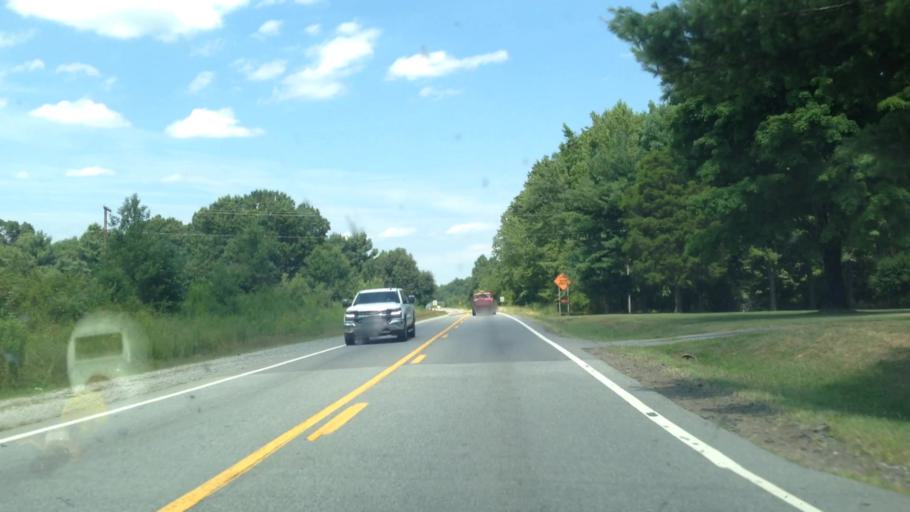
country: US
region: North Carolina
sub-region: Guilford County
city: Stokesdale
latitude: 36.2755
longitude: -79.9431
